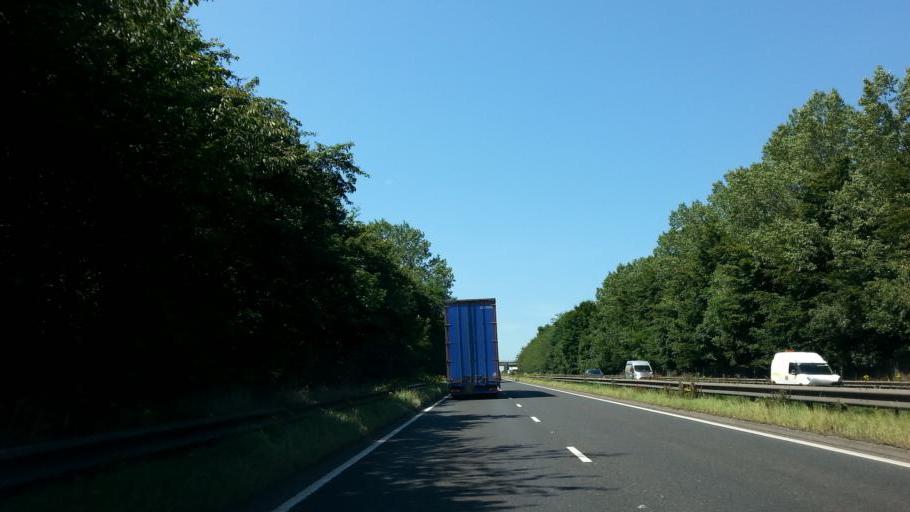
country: GB
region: England
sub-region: Derbyshire
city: Pinxton
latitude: 53.0932
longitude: -1.3398
